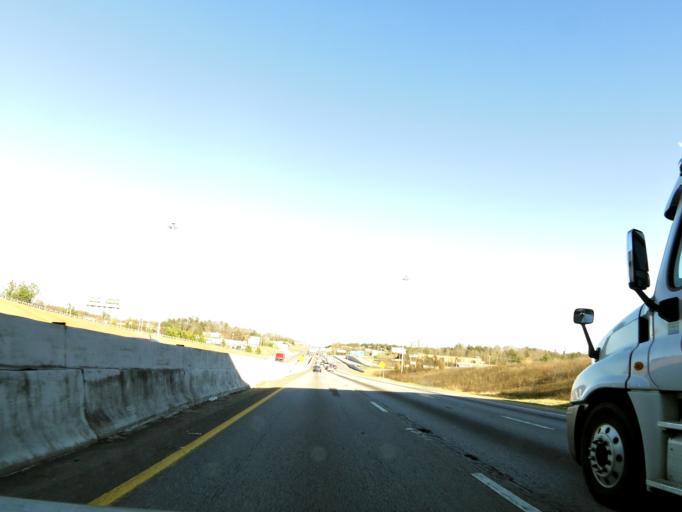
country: US
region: South Carolina
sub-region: Greenville County
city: Greer
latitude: 34.8722
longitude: -82.2244
